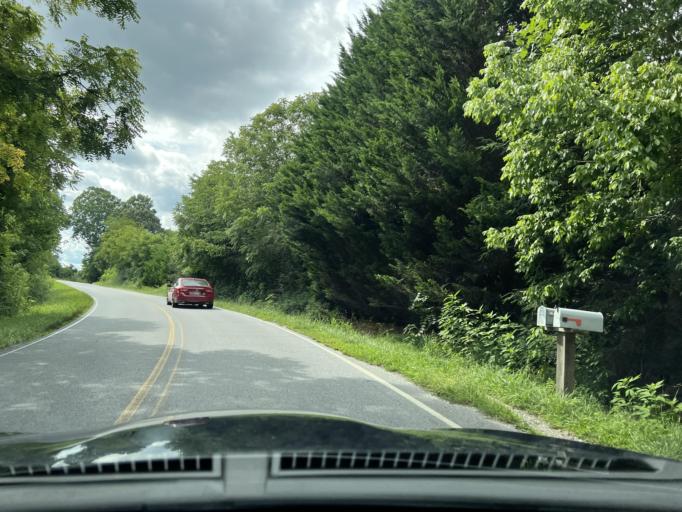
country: US
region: North Carolina
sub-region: Henderson County
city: Hoopers Creek
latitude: 35.4356
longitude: -82.4303
